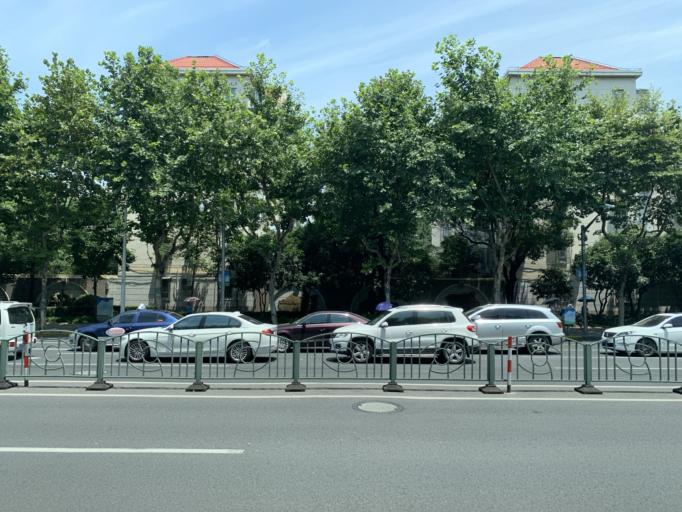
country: CN
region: Shanghai Shi
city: Pudong
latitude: 31.2367
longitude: 121.5181
